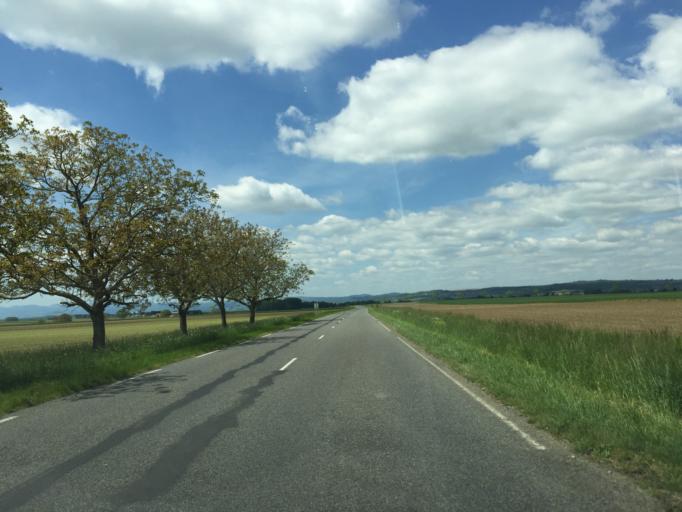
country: FR
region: Auvergne
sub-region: Departement du Puy-de-Dome
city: Aigueperse
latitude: 46.0246
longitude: 3.2410
